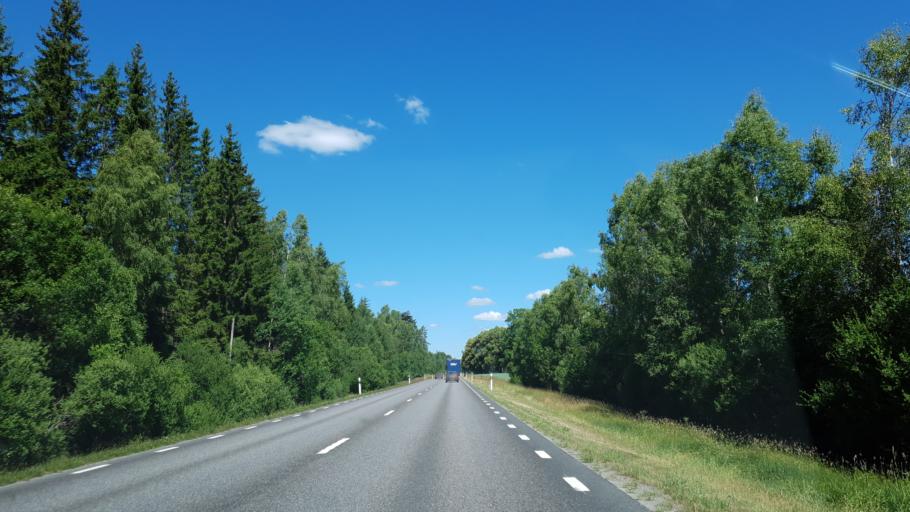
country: SE
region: Joenkoeping
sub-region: Varnamo Kommun
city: Rydaholm
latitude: 57.0162
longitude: 14.2594
